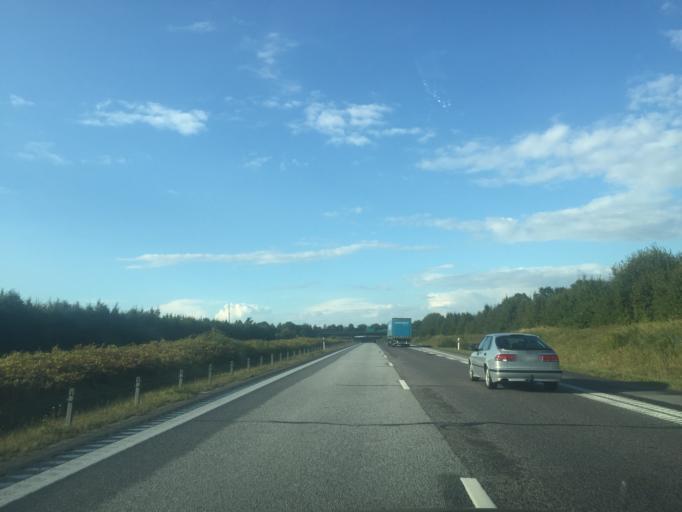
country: SE
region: Skane
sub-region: Burlovs Kommun
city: Arloev
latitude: 55.6334
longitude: 13.1083
